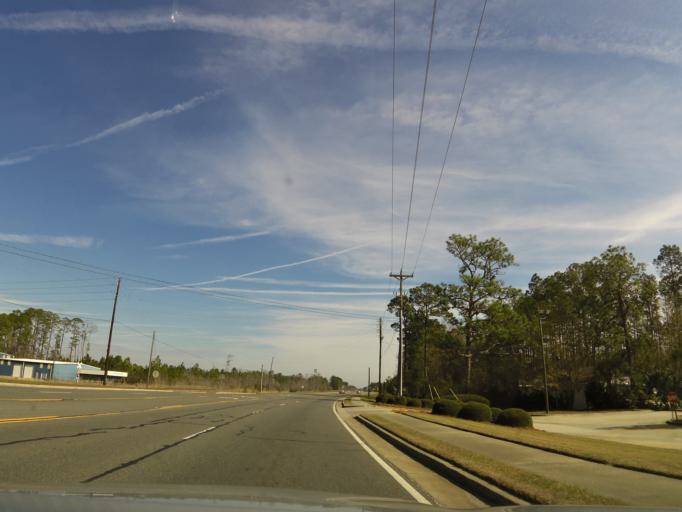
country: US
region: Georgia
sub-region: Brantley County
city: Nahunta
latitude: 31.2056
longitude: -81.9708
